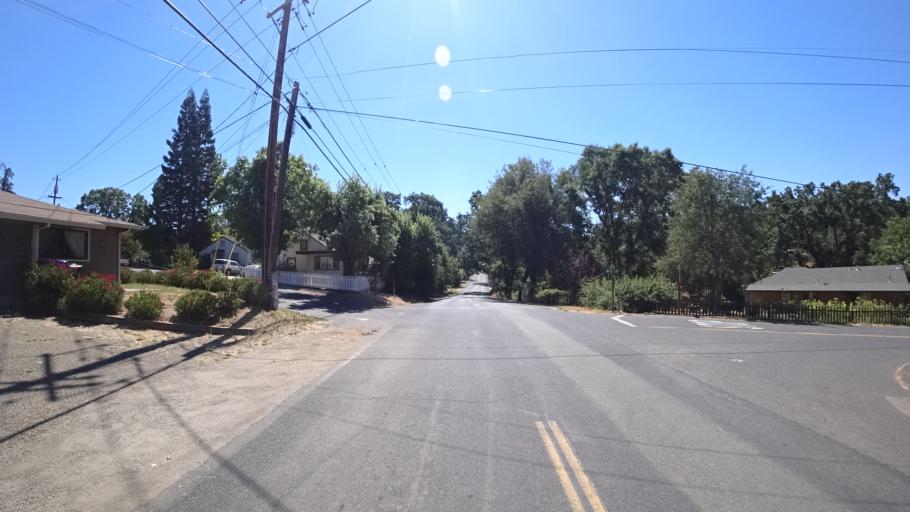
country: US
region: California
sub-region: Calaveras County
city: San Andreas
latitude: 38.1962
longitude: -120.6751
